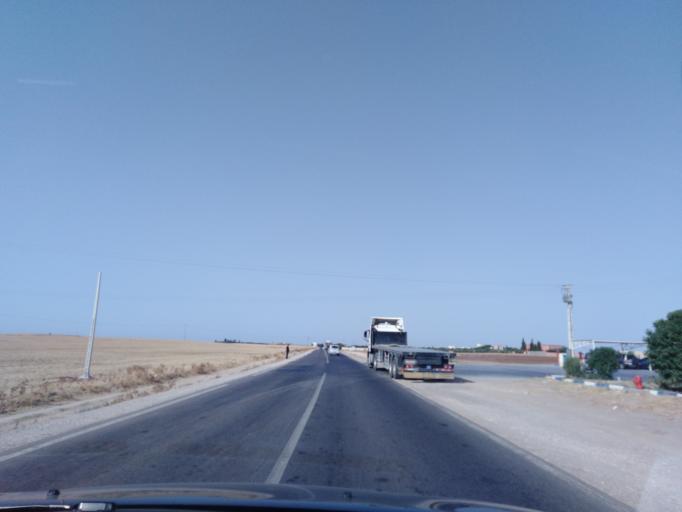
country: MA
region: Doukkala-Abda
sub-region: Safi
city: Safi
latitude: 32.2655
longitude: -8.9506
